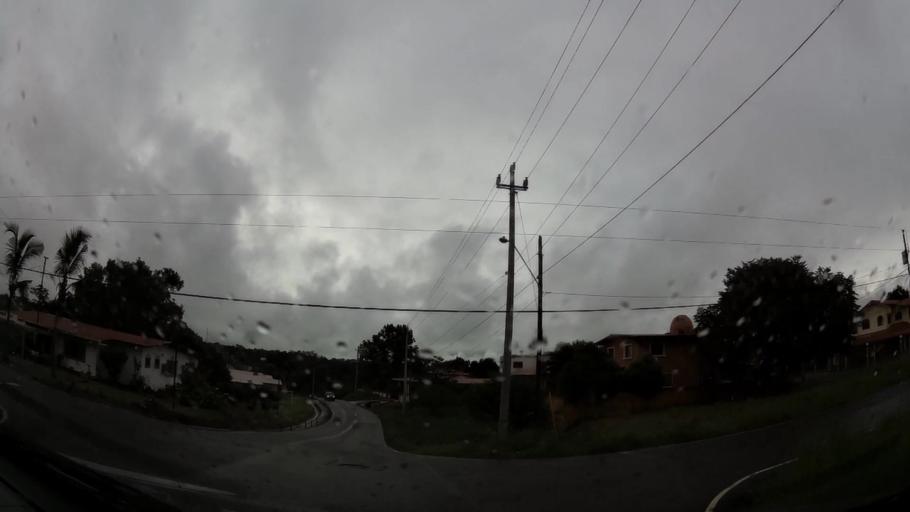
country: PA
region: Veraguas
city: Santiago de Veraguas
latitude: 8.0950
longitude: -80.9618
